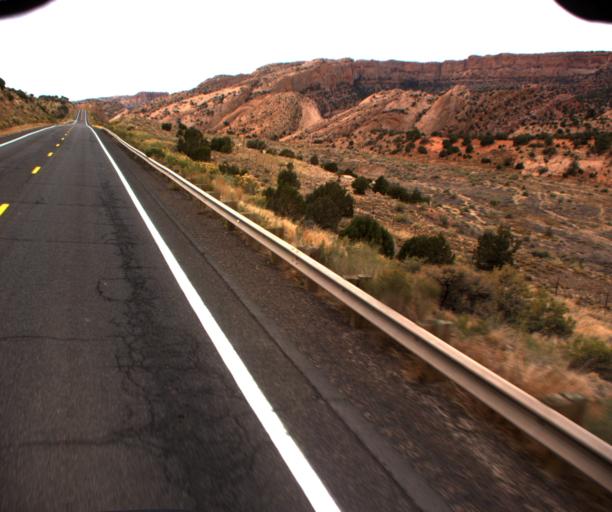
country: US
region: Arizona
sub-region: Navajo County
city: Kayenta
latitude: 36.6671
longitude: -110.4094
